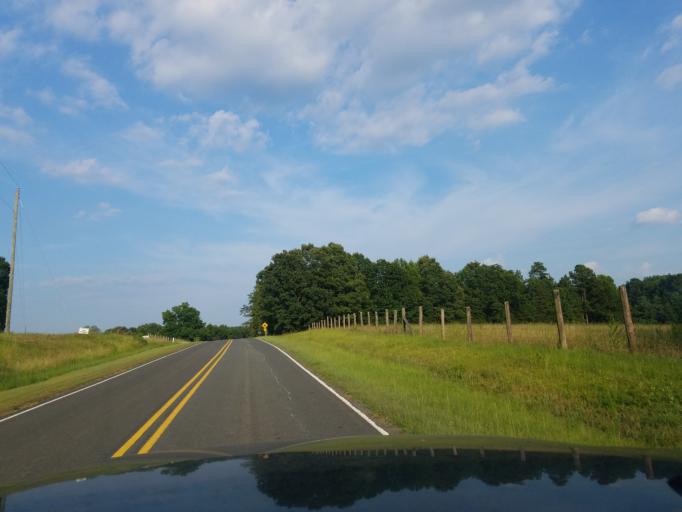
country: US
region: North Carolina
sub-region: Granville County
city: Butner
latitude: 36.1942
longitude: -78.8319
